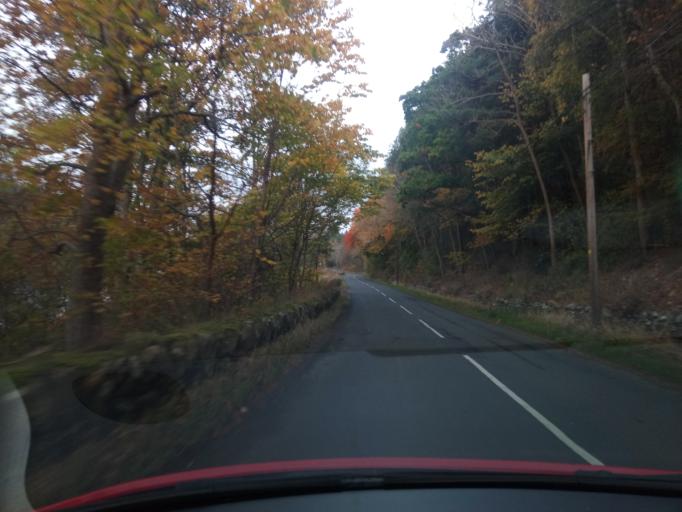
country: GB
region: Scotland
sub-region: The Scottish Borders
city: Selkirk
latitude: 55.6001
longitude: -2.8681
